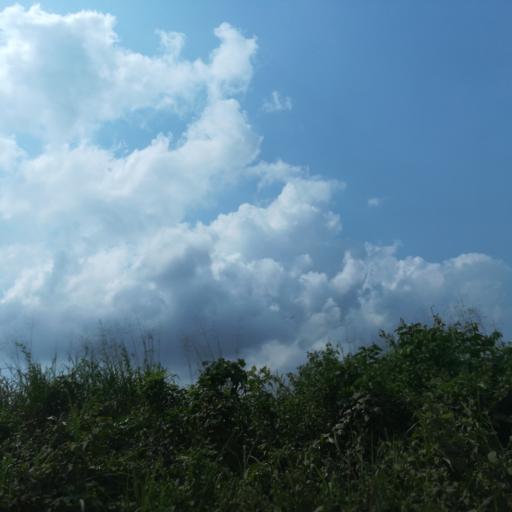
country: NG
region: Rivers
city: Okrika
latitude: 4.8051
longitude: 7.1034
